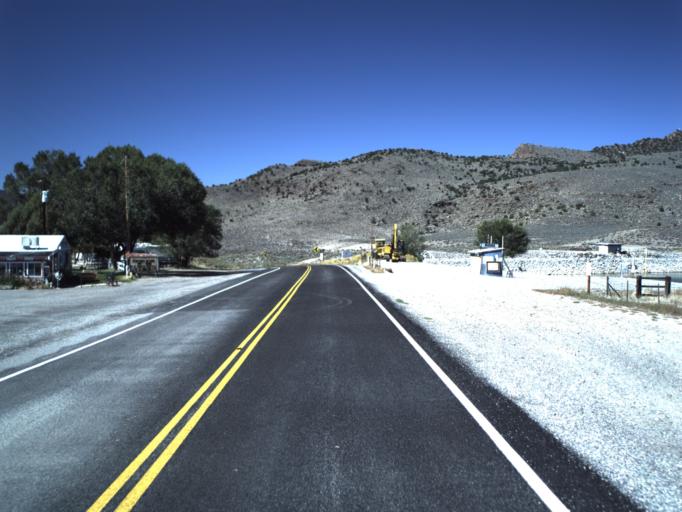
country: US
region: Utah
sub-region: Piute County
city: Junction
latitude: 38.1670
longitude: -112.0195
